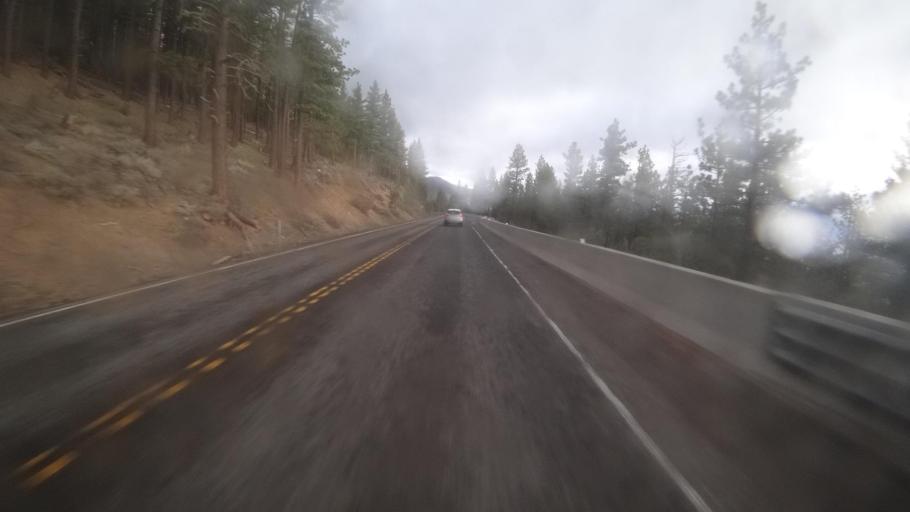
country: US
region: Nevada
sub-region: Washoe County
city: Incline Village
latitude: 39.3400
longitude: -119.8474
